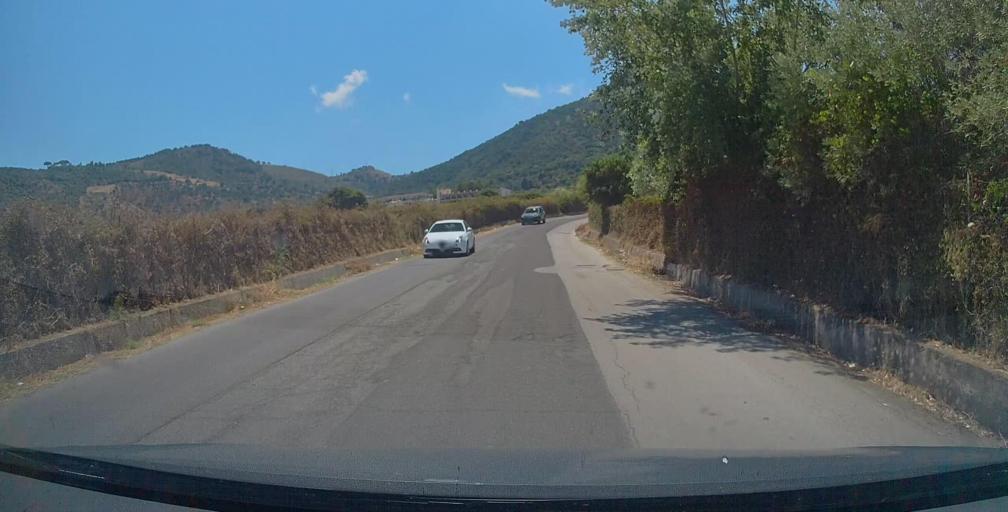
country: IT
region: Sicily
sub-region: Messina
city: Oliveri
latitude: 38.1439
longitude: 15.0153
